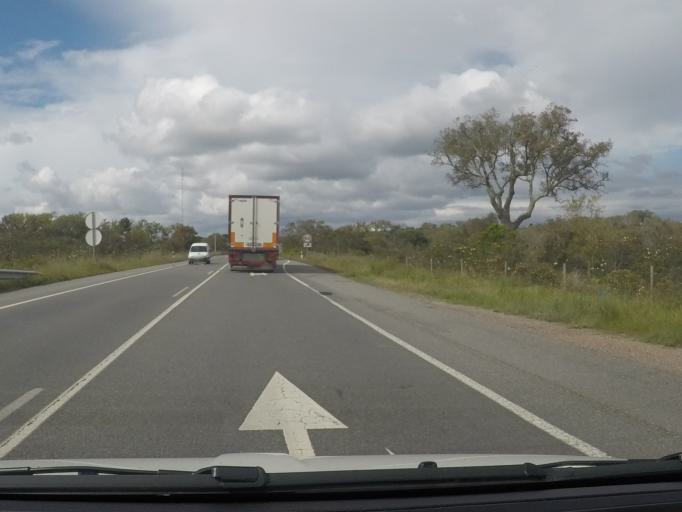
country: PT
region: Setubal
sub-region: Grandola
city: Grandola
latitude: 38.1528
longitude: -8.6495
